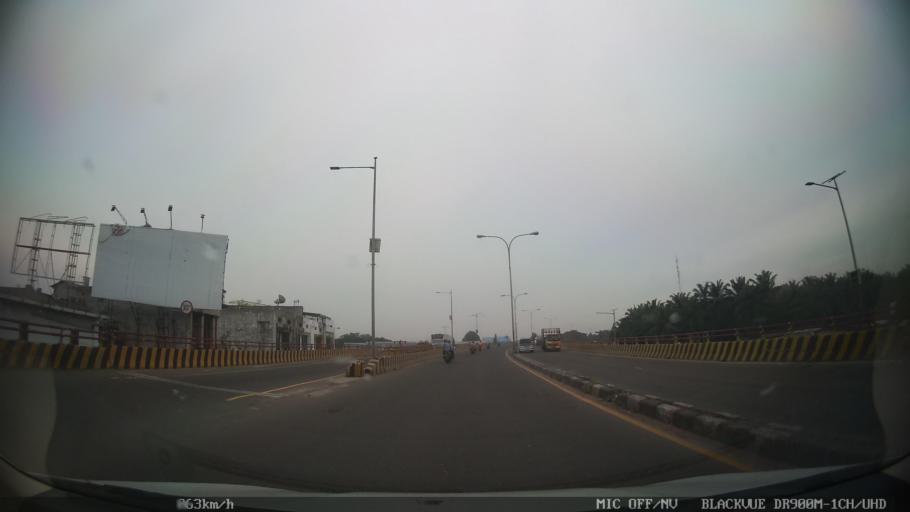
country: ID
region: North Sumatra
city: Deli Tua
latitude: 3.5362
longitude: 98.7189
